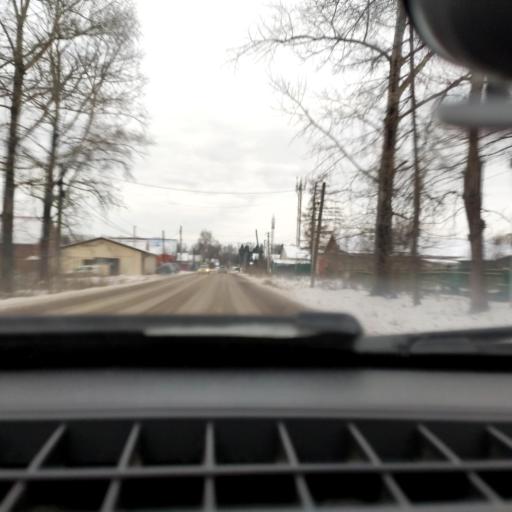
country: RU
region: Bashkortostan
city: Iglino
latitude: 54.8361
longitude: 56.4240
